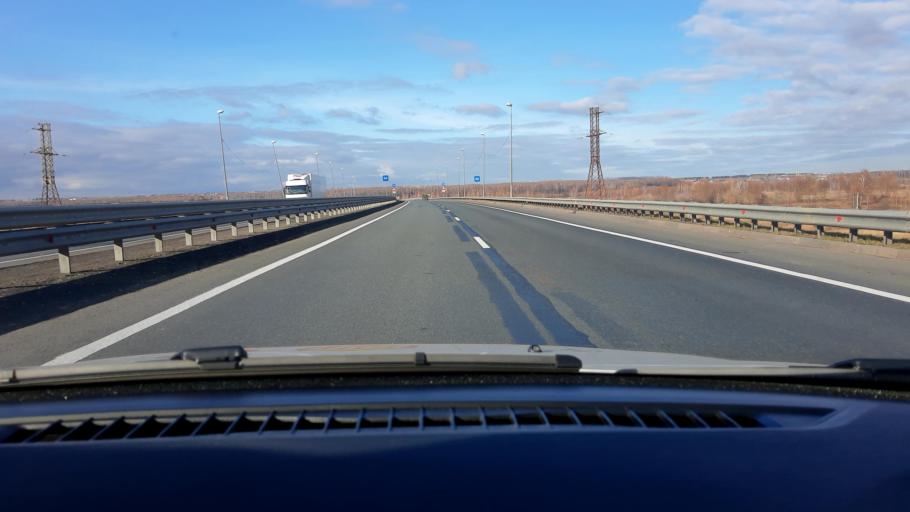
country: RU
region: Nizjnij Novgorod
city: Burevestnik
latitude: 56.1205
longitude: 43.8129
